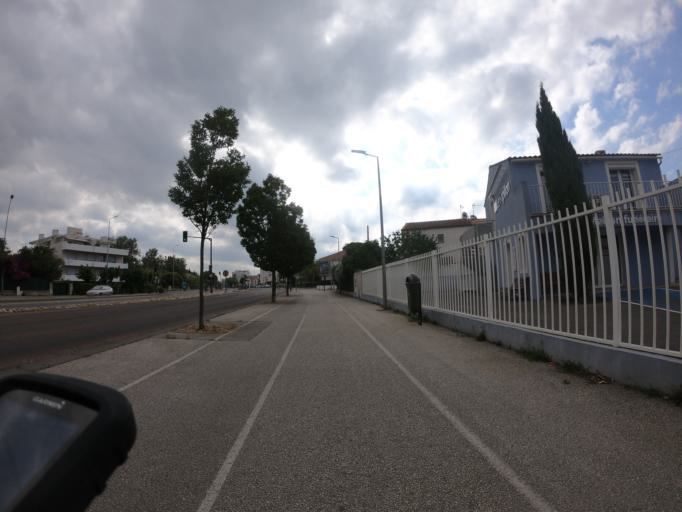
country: FR
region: Provence-Alpes-Cote d'Azur
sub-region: Departement du Var
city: La Seyne-sur-Mer
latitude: 43.1066
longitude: 5.8722
